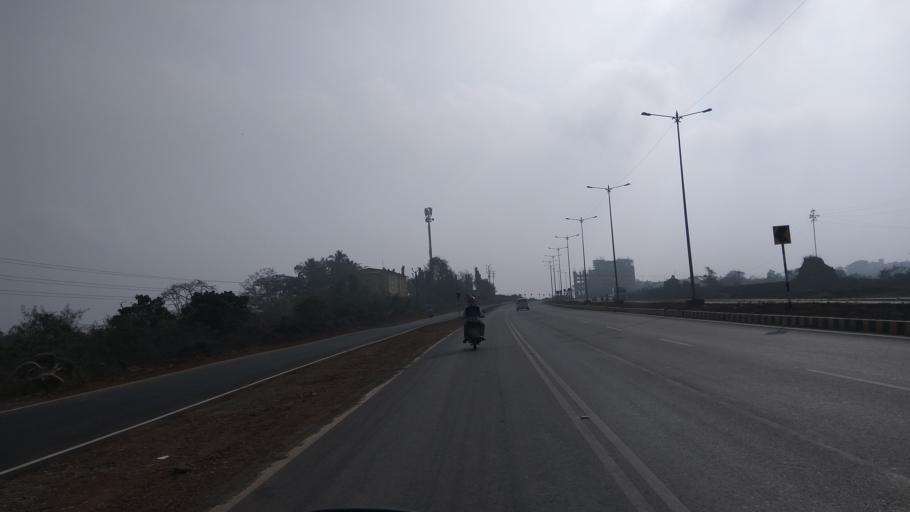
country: IN
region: Goa
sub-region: North Goa
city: Bambolim
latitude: 15.4995
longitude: 73.8714
